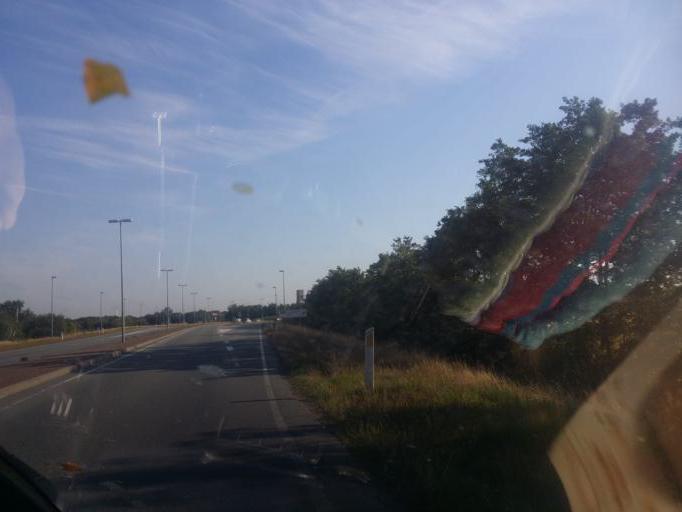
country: DK
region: South Denmark
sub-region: Esbjerg Kommune
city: Ribe
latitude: 55.3191
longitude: 8.7533
